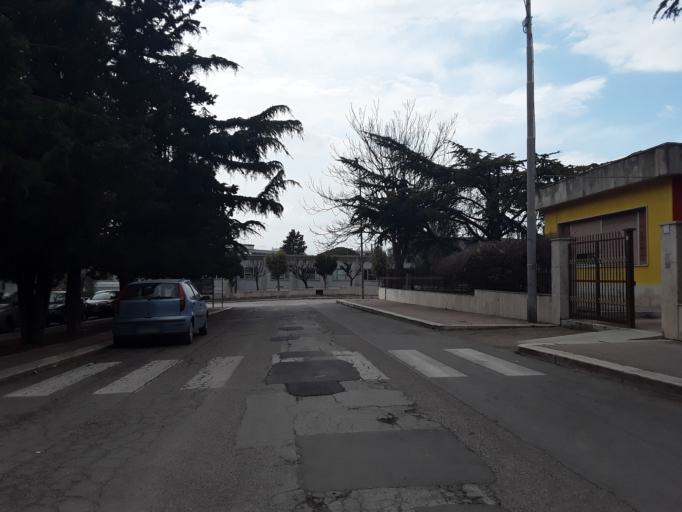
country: IT
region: Apulia
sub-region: Provincia di Bari
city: Ruvo di Puglia
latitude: 41.1206
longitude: 16.4806
